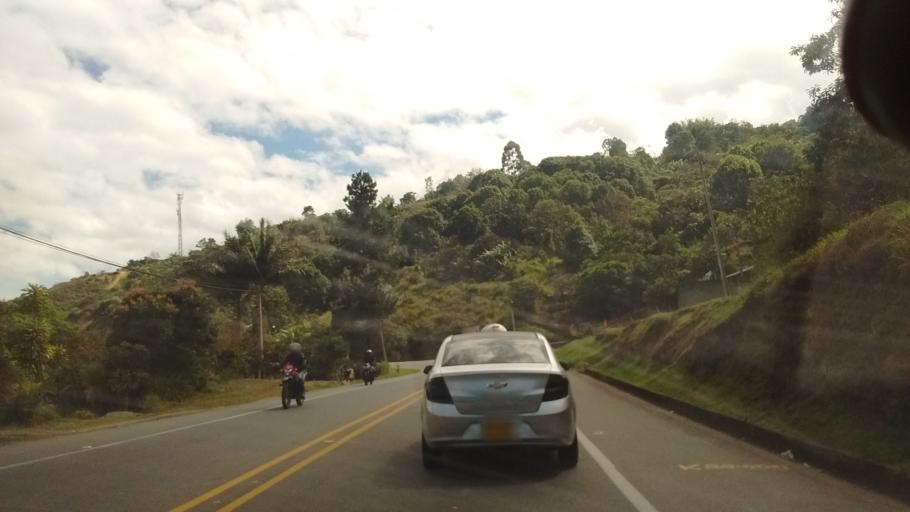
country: CO
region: Cauca
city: Cajibio
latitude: 2.6279
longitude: -76.5244
